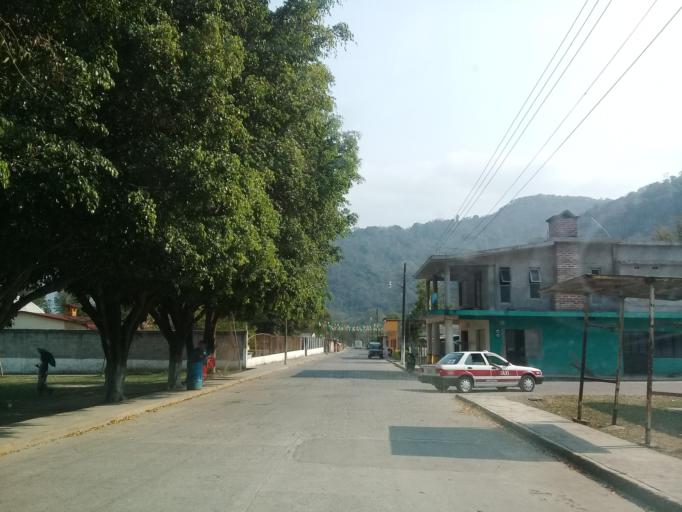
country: MX
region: Veracruz
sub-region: Ixtaczoquitlan
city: Campo Chico
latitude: 18.8374
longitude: -97.0297
